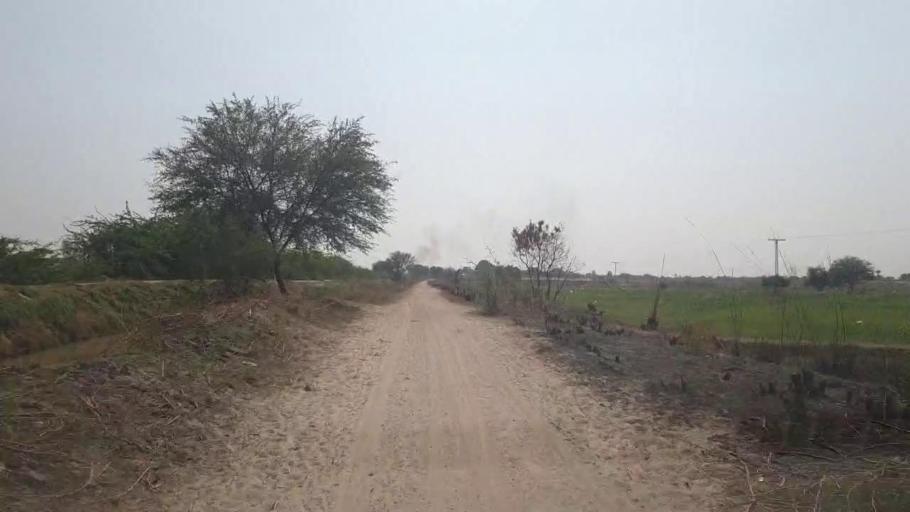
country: PK
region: Sindh
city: Dhoro Naro
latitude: 25.5077
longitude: 69.5431
